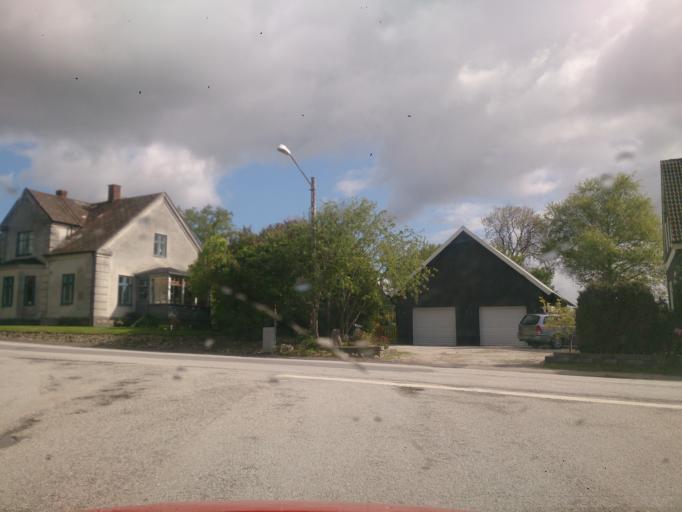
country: SE
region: Skane
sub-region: Ystads Kommun
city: Ystad
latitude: 55.4873
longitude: 13.7135
